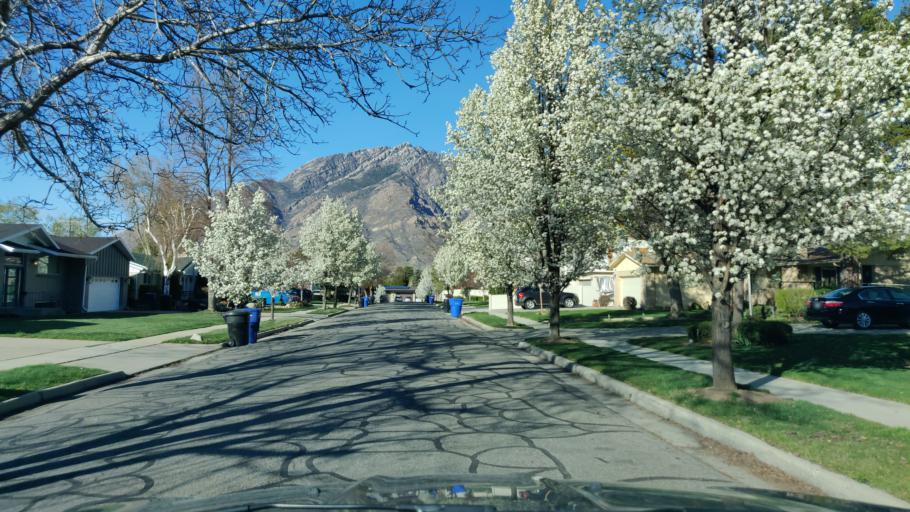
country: US
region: Utah
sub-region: Salt Lake County
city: Cottonwood Heights
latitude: 40.6181
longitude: -111.8212
